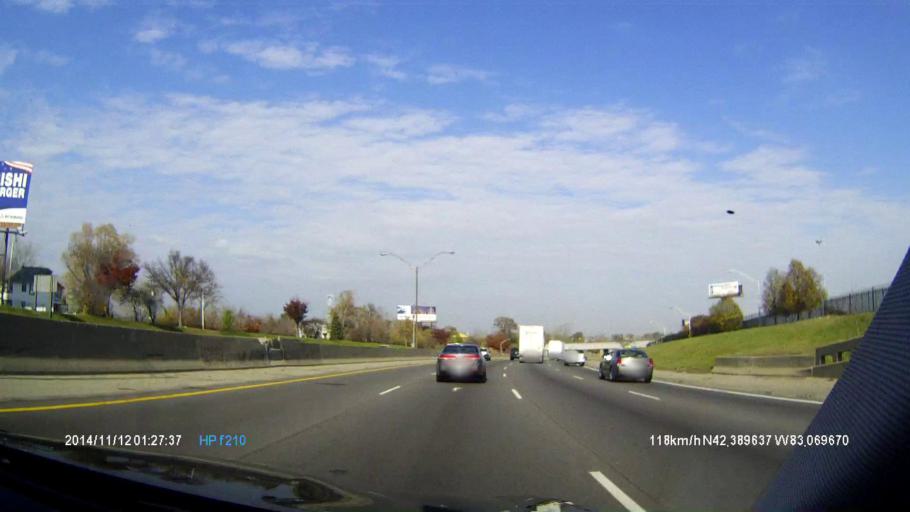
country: US
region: Michigan
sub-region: Wayne County
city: Hamtramck
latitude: 42.3898
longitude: -83.0697
